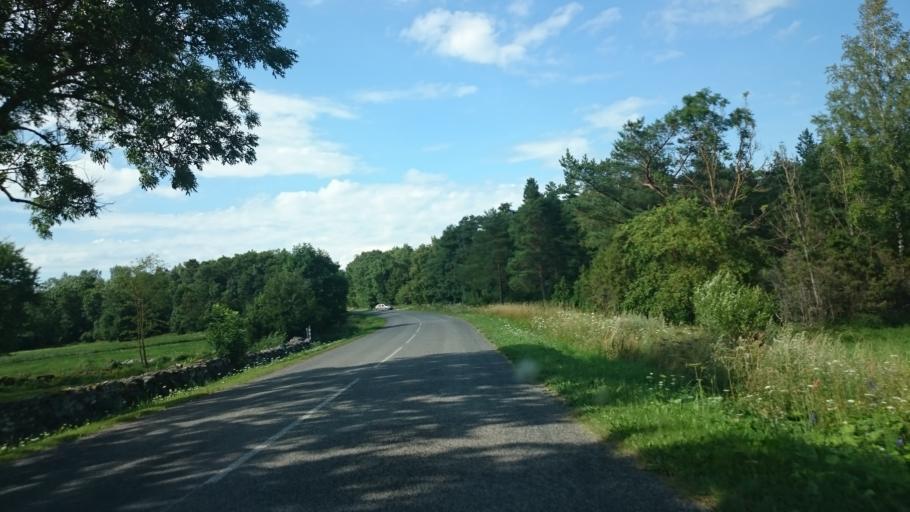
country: EE
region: Saare
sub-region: Orissaare vald
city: Orissaare
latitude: 58.6010
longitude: 22.9769
